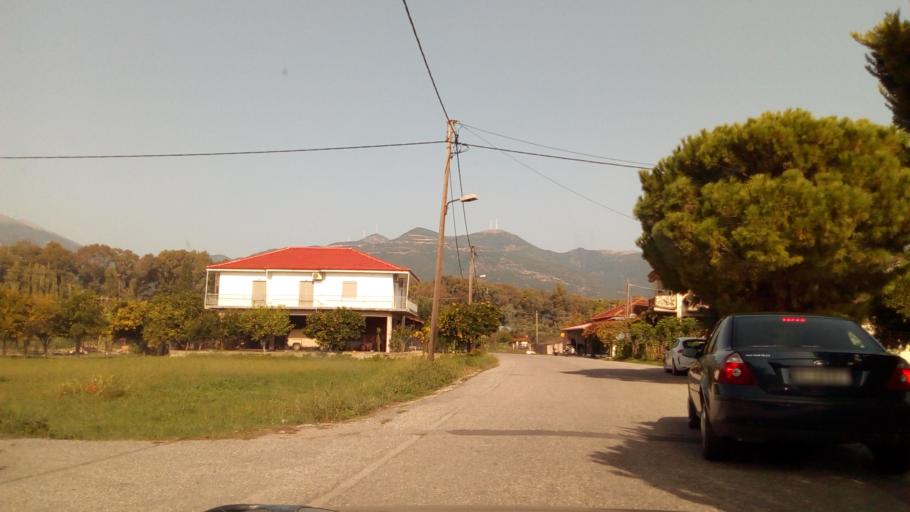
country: GR
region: West Greece
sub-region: Nomos Aitolias kai Akarnanias
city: Nafpaktos
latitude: 38.3958
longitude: 21.8720
